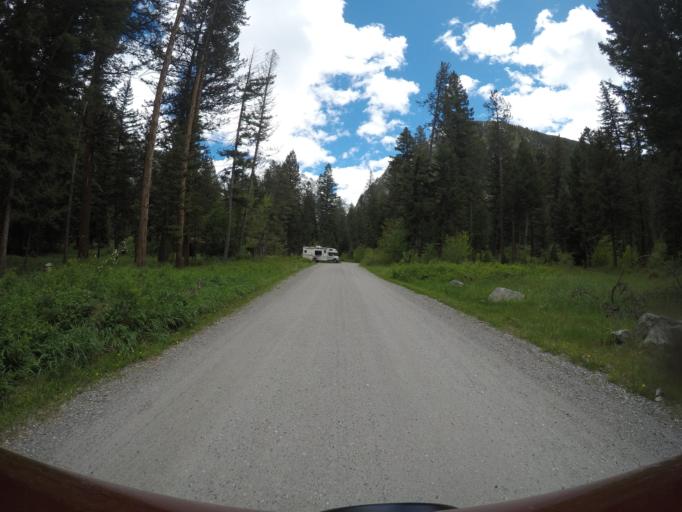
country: US
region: Montana
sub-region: Park County
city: Livingston
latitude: 45.4979
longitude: -110.5220
